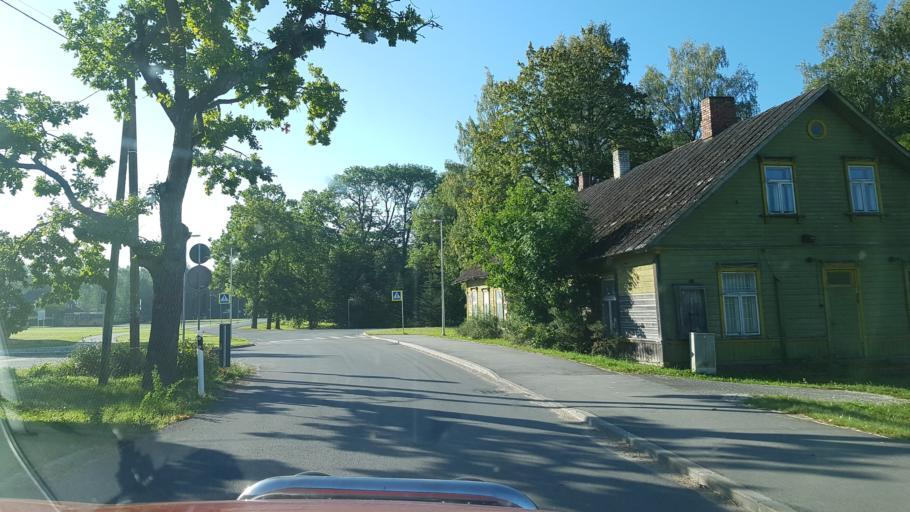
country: EE
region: Jogevamaa
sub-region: Tabivere vald
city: Tabivere
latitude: 58.6858
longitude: 26.5841
